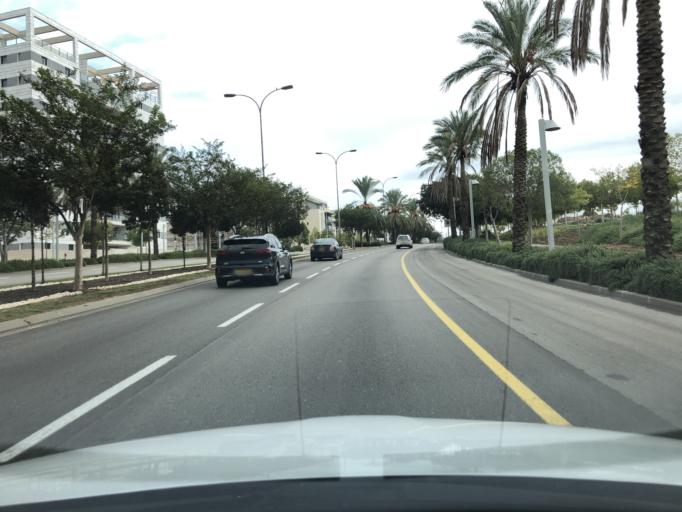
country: IL
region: Central District
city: Modiin
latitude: 31.9096
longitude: 35.0084
